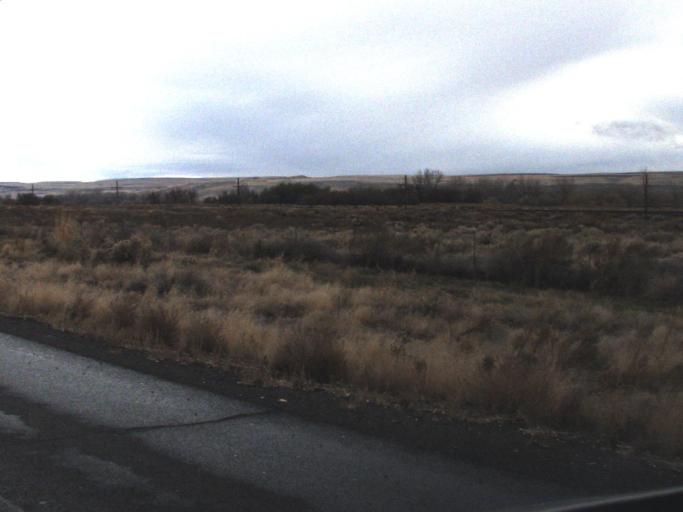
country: US
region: Washington
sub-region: Walla Walla County
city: Burbank
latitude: 46.1474
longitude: -118.9386
